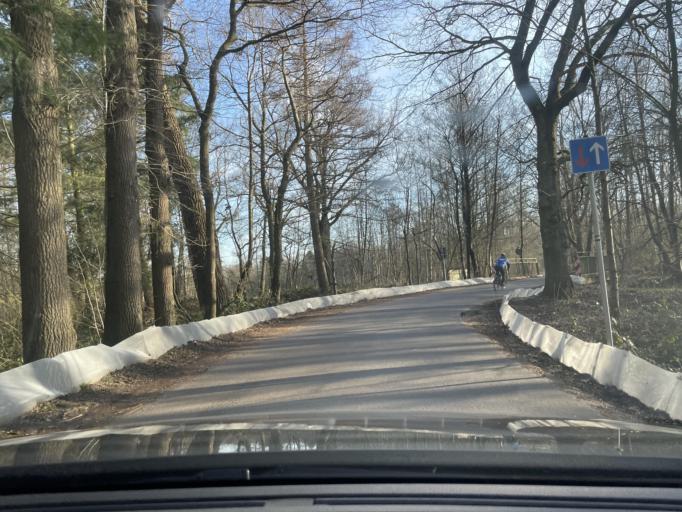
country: DE
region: North Rhine-Westphalia
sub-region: Regierungsbezirk Dusseldorf
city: Bruggen
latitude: 51.2382
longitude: 6.1522
